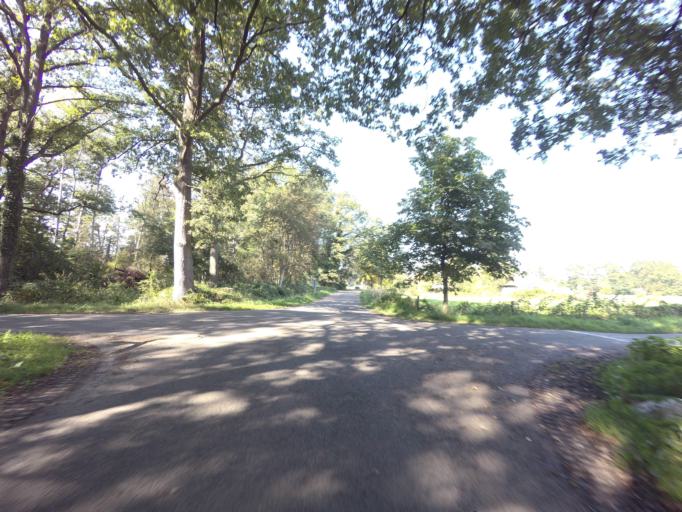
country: NL
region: Overijssel
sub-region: Gemeente Haaksbergen
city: Haaksbergen
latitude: 52.2027
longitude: 6.7768
